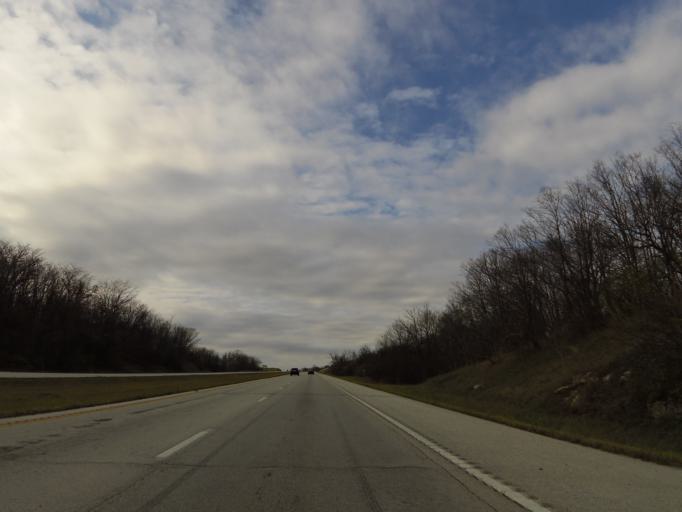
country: US
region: Missouri
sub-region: Marion County
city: Hannibal
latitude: 39.7385
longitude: -91.4139
